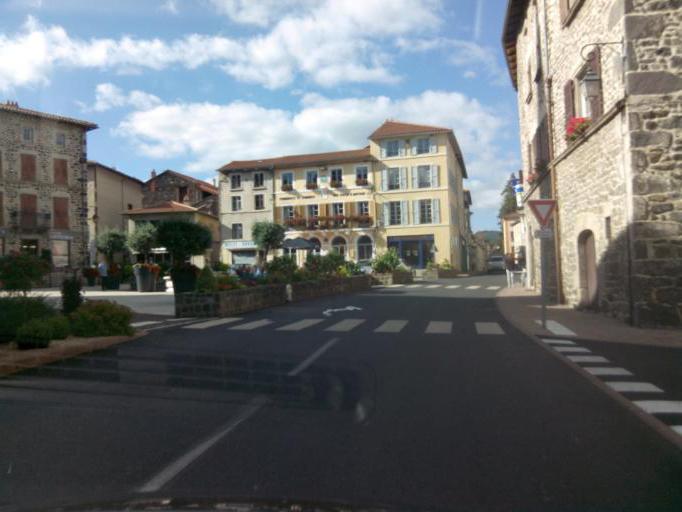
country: FR
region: Auvergne
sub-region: Departement de la Haute-Loire
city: Saint-Paulien
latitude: 45.1341
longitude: 3.8133
